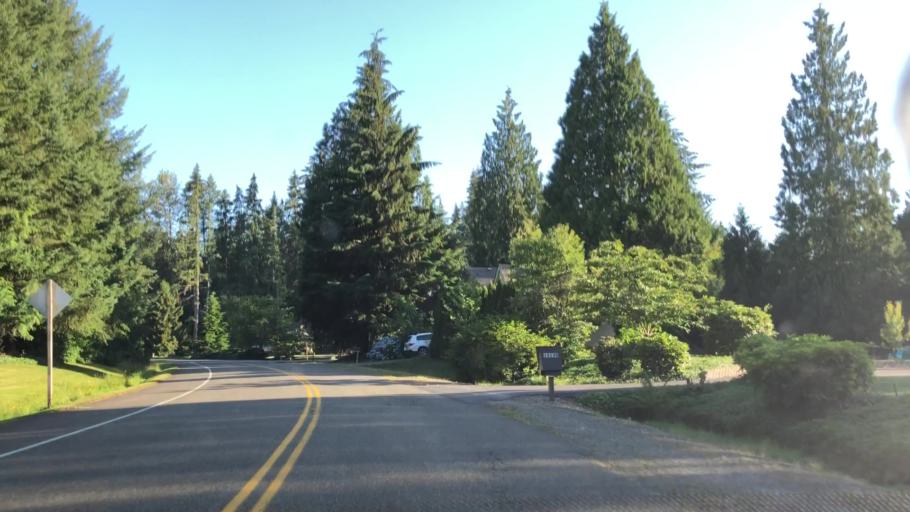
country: US
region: Washington
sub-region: King County
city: Cottage Lake
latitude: 47.7372
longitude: -122.0919
